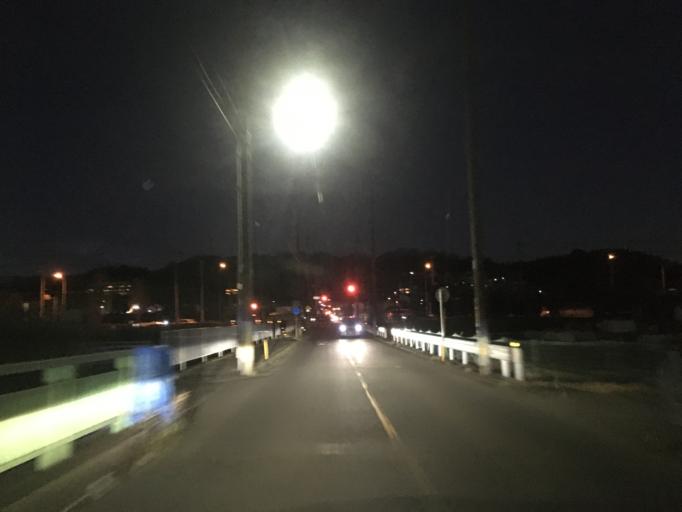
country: JP
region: Tokyo
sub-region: Machida-shi
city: Machida
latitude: 35.5590
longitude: 139.5240
